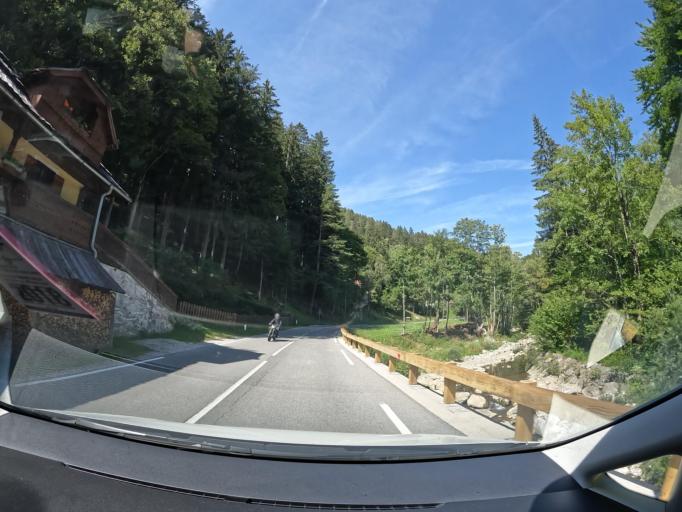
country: SI
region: Zirovnica
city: Zirovnica
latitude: 46.4387
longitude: 14.2014
